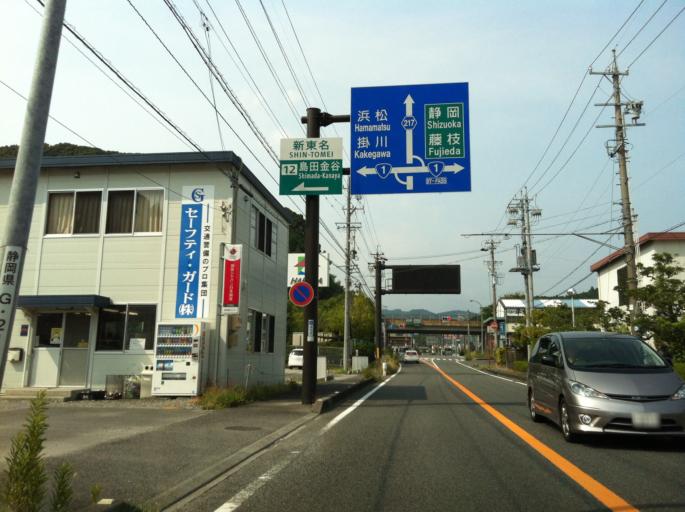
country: JP
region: Shizuoka
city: Shimada
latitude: 34.8468
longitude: 138.1823
